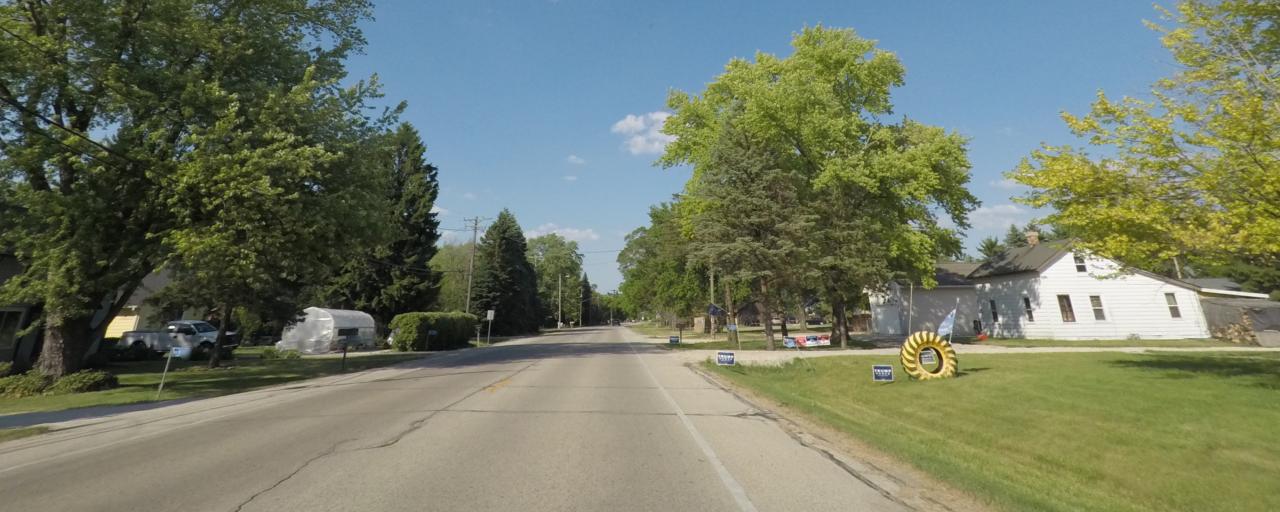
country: US
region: Wisconsin
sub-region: Waukesha County
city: Big Bend
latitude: 42.8830
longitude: -88.2007
